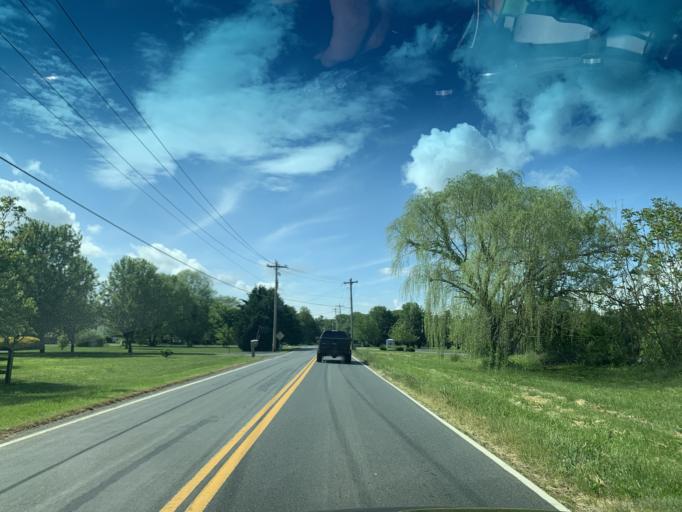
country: US
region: Maryland
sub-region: Cecil County
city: Rising Sun
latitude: 39.7068
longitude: -76.1462
